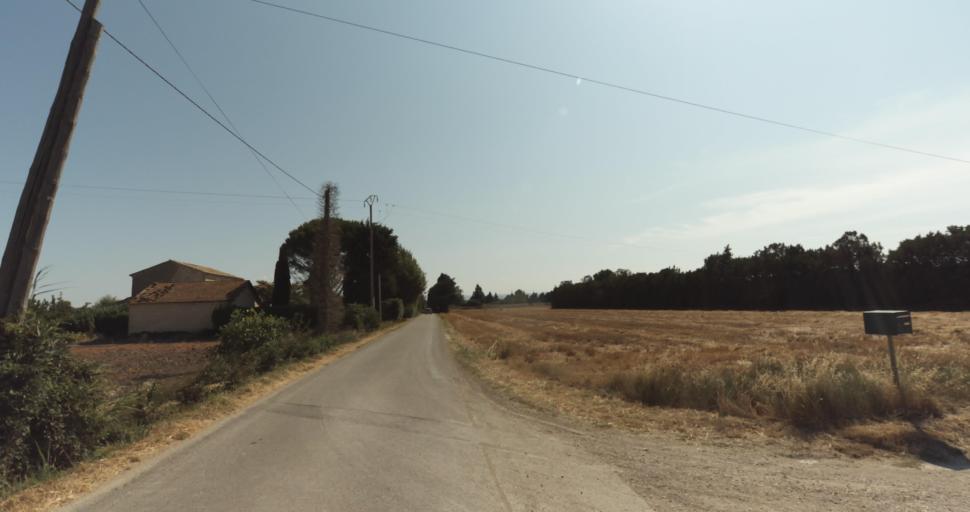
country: FR
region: Provence-Alpes-Cote d'Azur
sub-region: Departement du Vaucluse
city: Althen-des-Paluds
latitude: 44.0126
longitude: 4.9756
